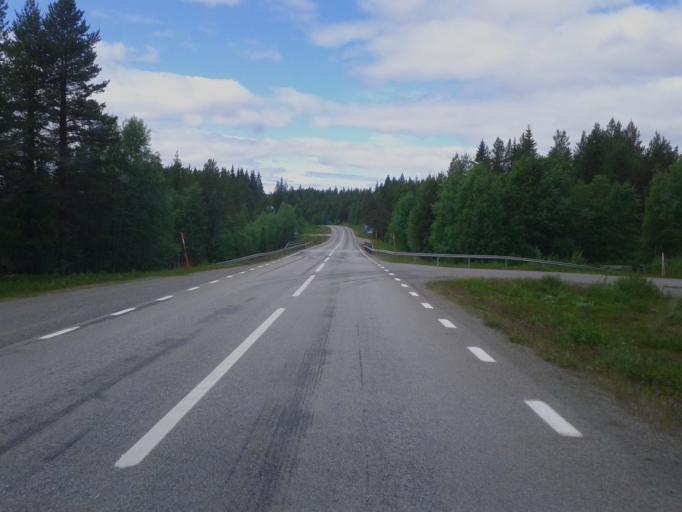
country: SE
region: Vaesterbotten
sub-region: Storumans Kommun
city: Fristad
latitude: 65.3825
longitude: 16.5078
